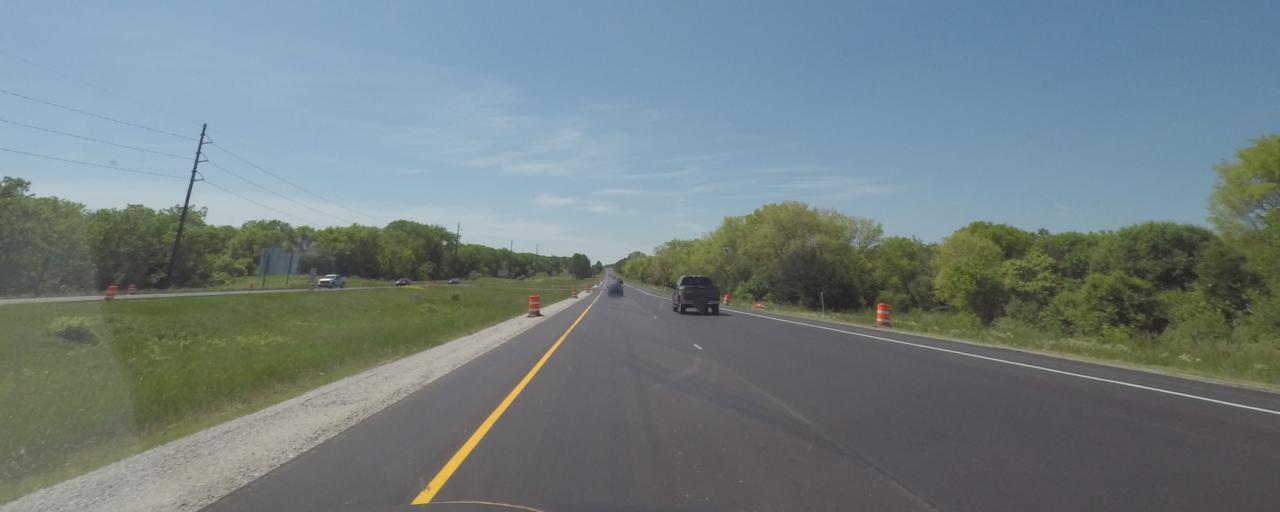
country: US
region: Wisconsin
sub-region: Jefferson County
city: Lake Mills
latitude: 43.0948
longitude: -88.9131
